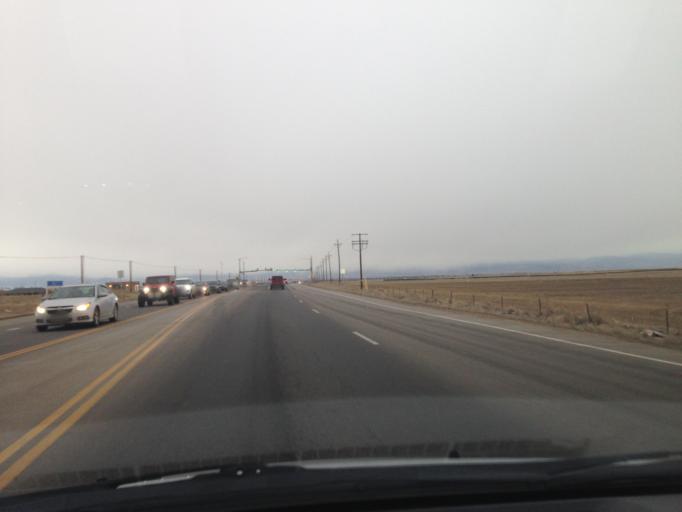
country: US
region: Colorado
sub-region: Weld County
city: Dacono
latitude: 40.0878
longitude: -104.9457
